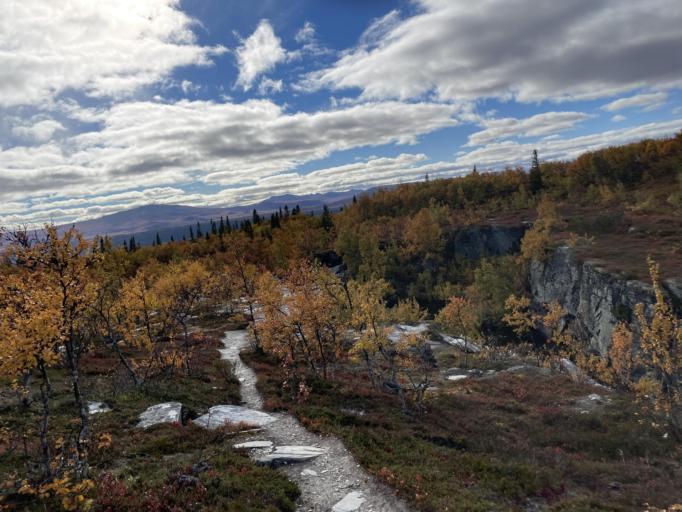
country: SE
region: Jaemtland
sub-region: Are Kommun
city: Are
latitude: 62.6917
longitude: 12.9093
